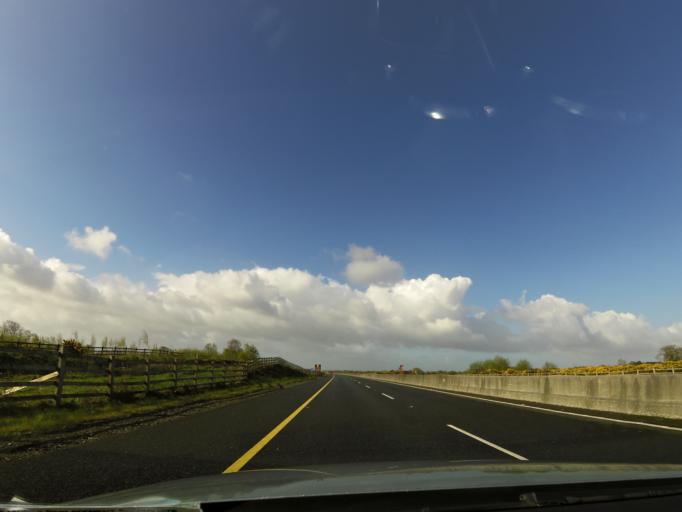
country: IE
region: Munster
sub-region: County Limerick
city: Castleconnell
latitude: 52.7244
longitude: -8.4663
